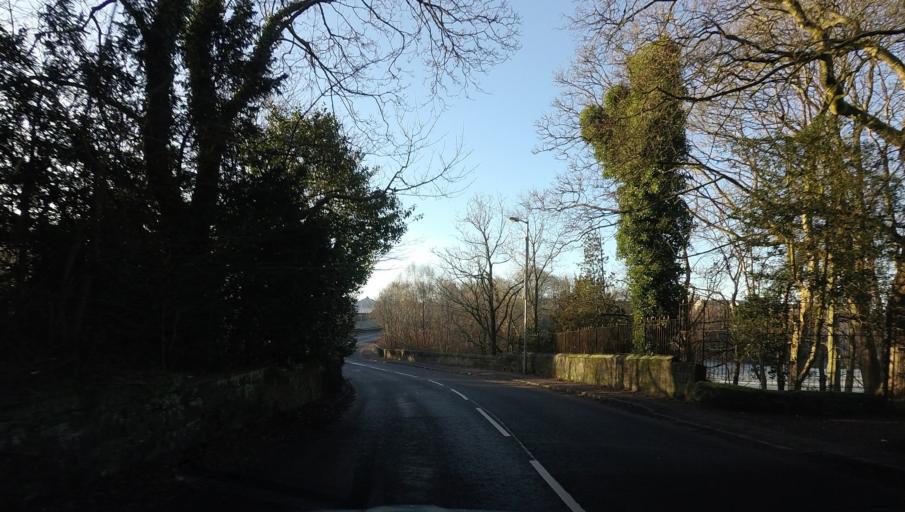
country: GB
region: Scotland
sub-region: North Lanarkshire
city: Newmains
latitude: 55.7900
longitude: -3.8620
